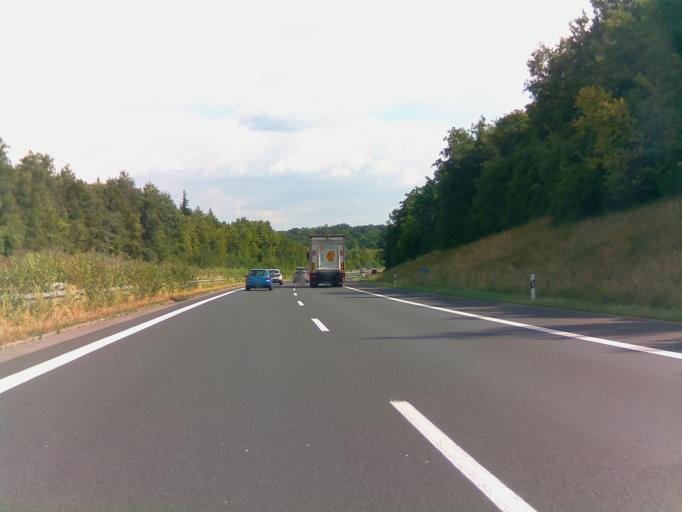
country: DE
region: Bavaria
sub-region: Regierungsbezirk Unterfranken
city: Kurnach
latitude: 49.8289
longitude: 10.0408
